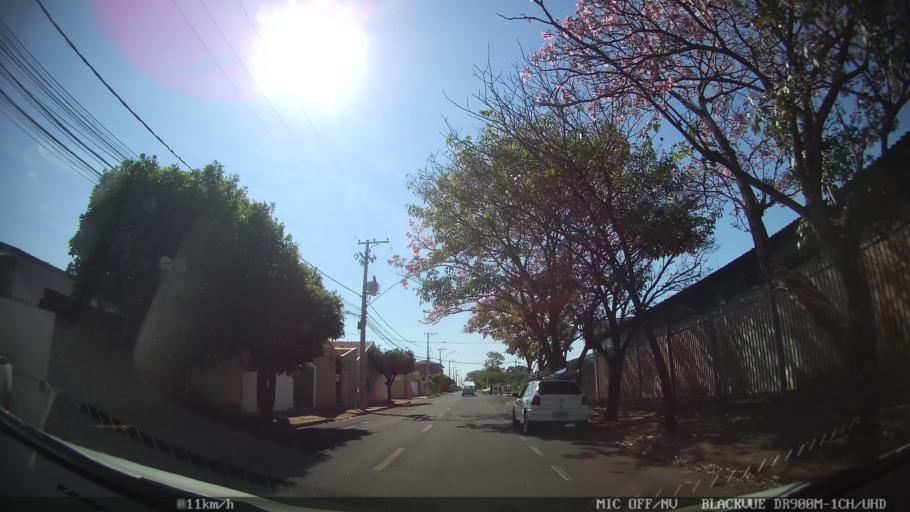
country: BR
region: Sao Paulo
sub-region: Sao Jose Do Rio Preto
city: Sao Jose do Rio Preto
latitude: -20.7795
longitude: -49.4197
